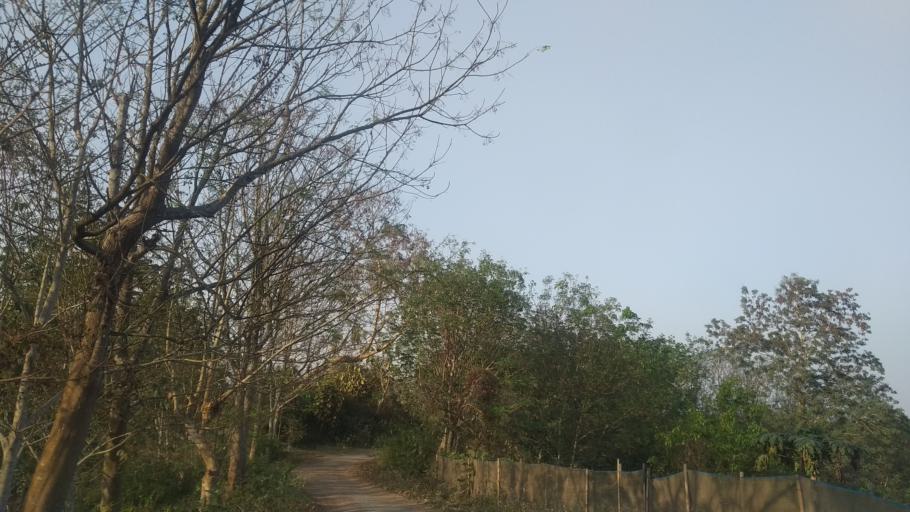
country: IN
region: Tripura
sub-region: West Tripura
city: Sonamura
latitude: 23.4379
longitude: 91.3610
